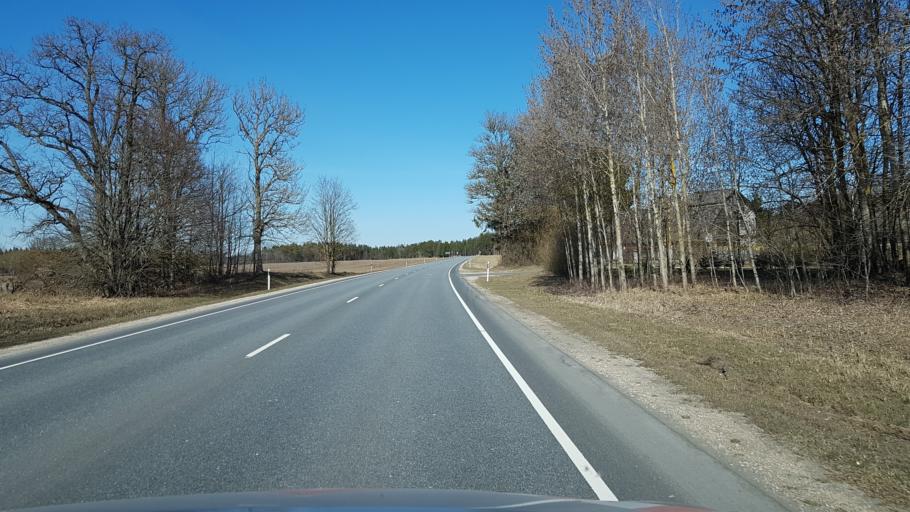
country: EE
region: Harju
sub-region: Nissi vald
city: Turba
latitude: 59.0175
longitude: 24.1407
